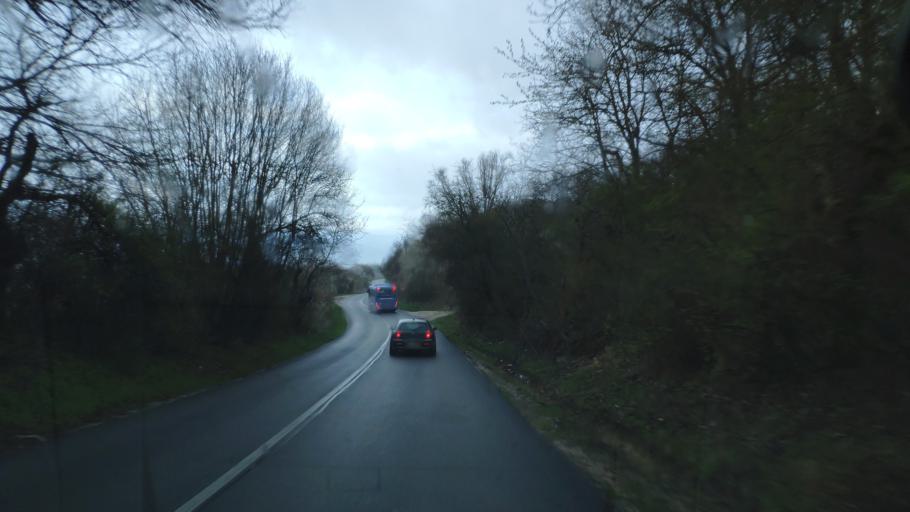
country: SK
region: Trenciansky
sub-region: Okres Nove Mesto nad Vahom
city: Nove Mesto nad Vahom
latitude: 48.7747
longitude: 17.8110
